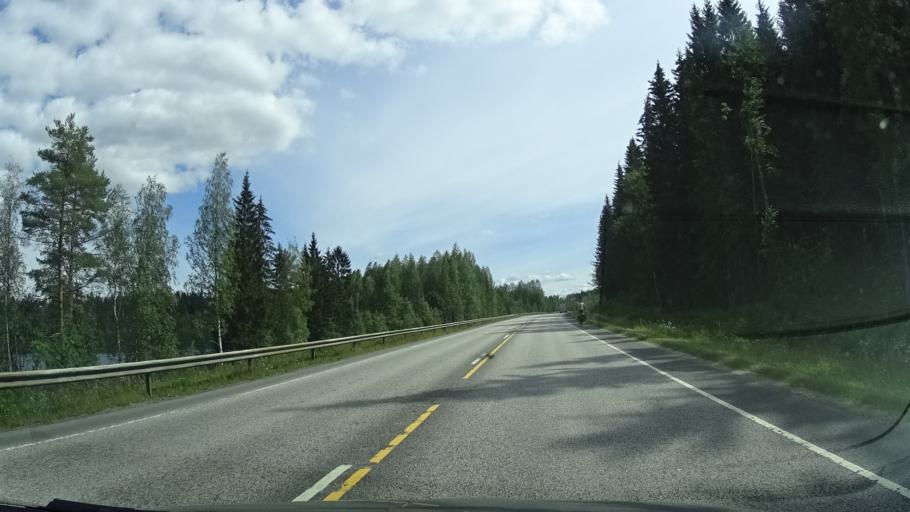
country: FI
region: Central Finland
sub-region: Jyvaeskylae
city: Jyvaeskylae
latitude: 62.2565
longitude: 25.6184
